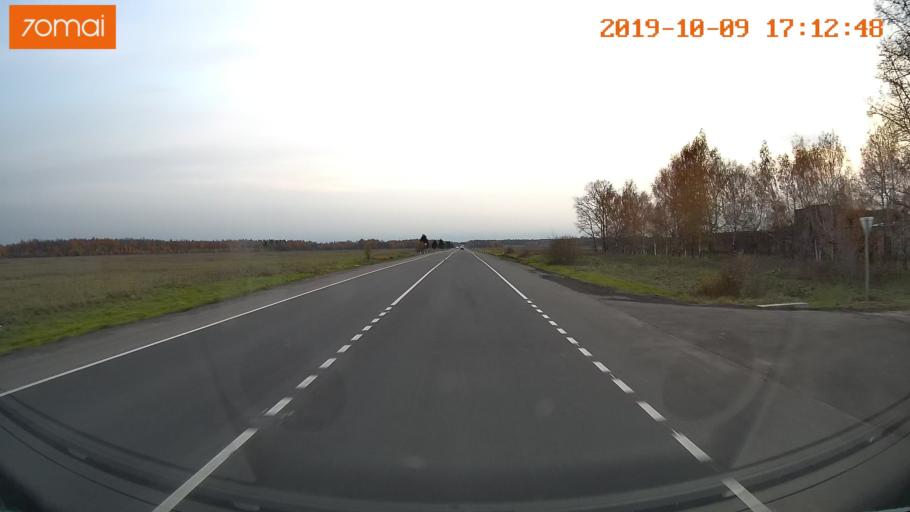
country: RU
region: Ivanovo
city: Privolzhsk
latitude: 57.3236
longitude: 41.2353
